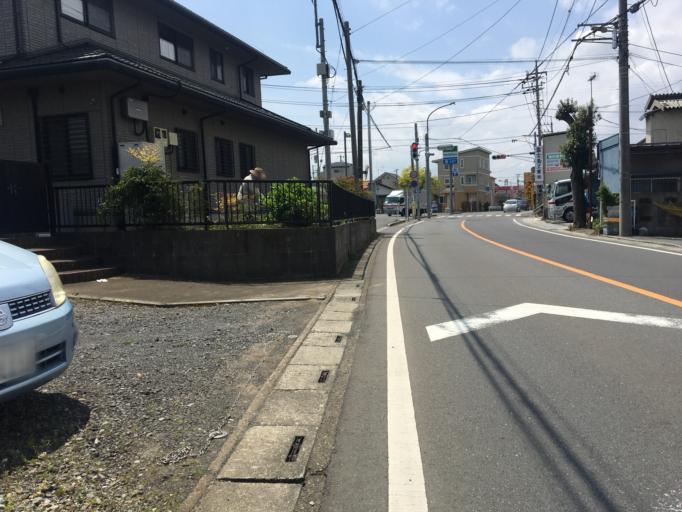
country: JP
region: Saitama
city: Shiki
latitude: 35.8424
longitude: 139.5630
